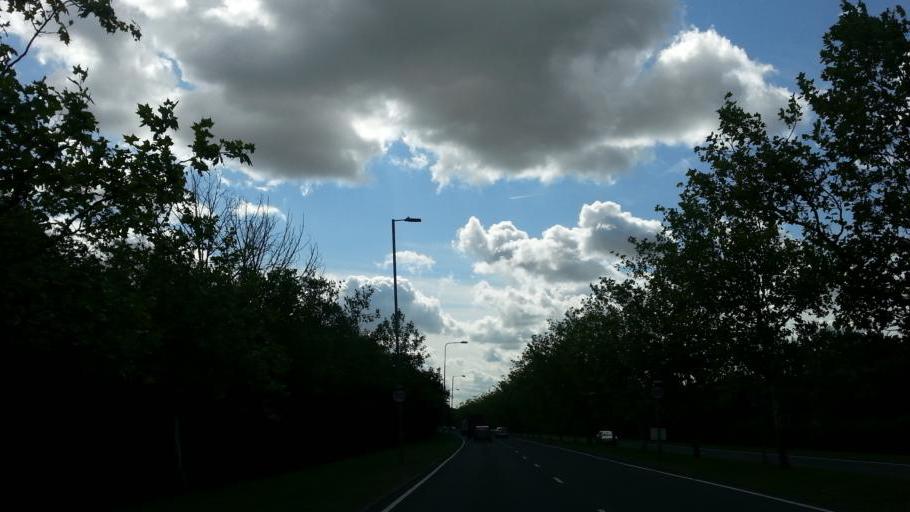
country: GB
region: England
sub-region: Essex
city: Basildon
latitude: 51.5778
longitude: 0.4442
